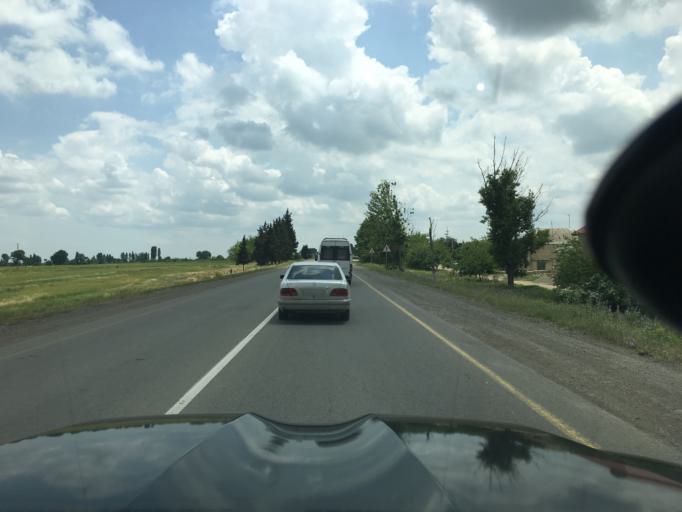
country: AZ
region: Tovuz
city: Tovuz
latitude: 40.9549
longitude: 45.7386
